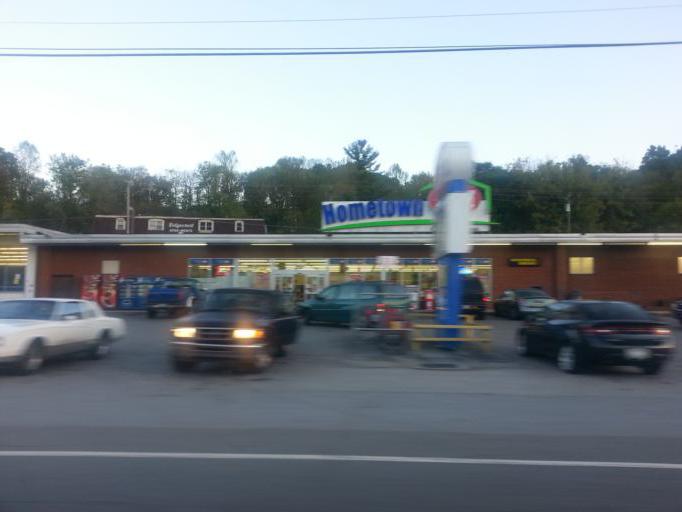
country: US
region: Tennessee
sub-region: Campbell County
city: Hunter
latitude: 36.3672
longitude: -84.1352
